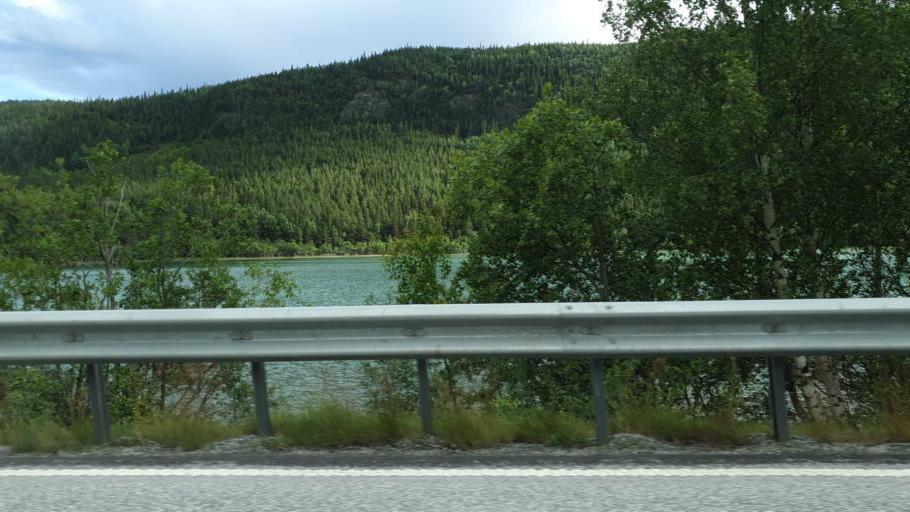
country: NO
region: Oppland
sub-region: Vaga
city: Vagamo
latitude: 61.8742
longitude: 9.1738
